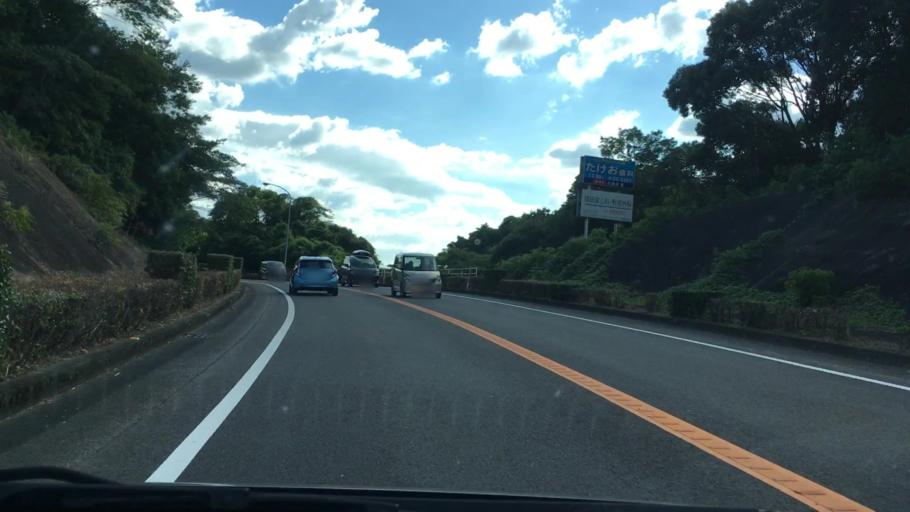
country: JP
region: Saga Prefecture
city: Takeocho-takeo
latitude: 33.1957
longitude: 129.9690
